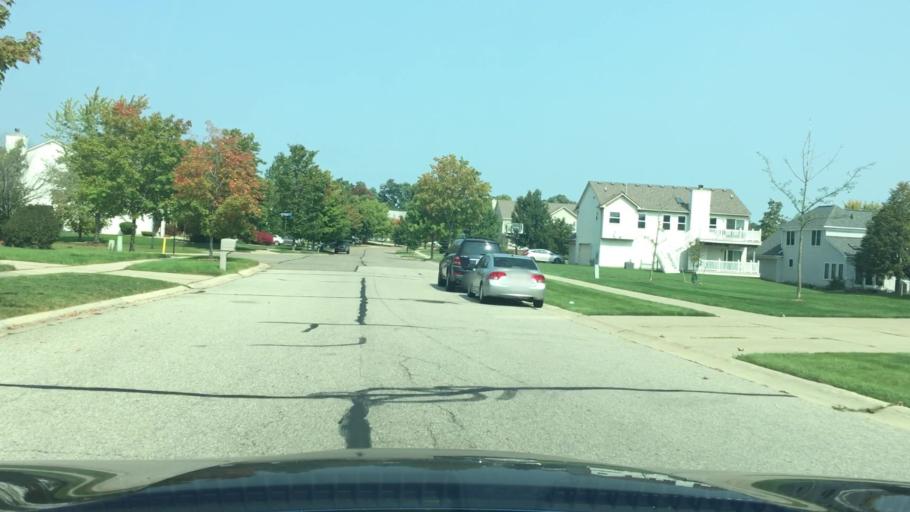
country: US
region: Michigan
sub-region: Washtenaw County
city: Ypsilanti
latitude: 42.2126
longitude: -83.6690
